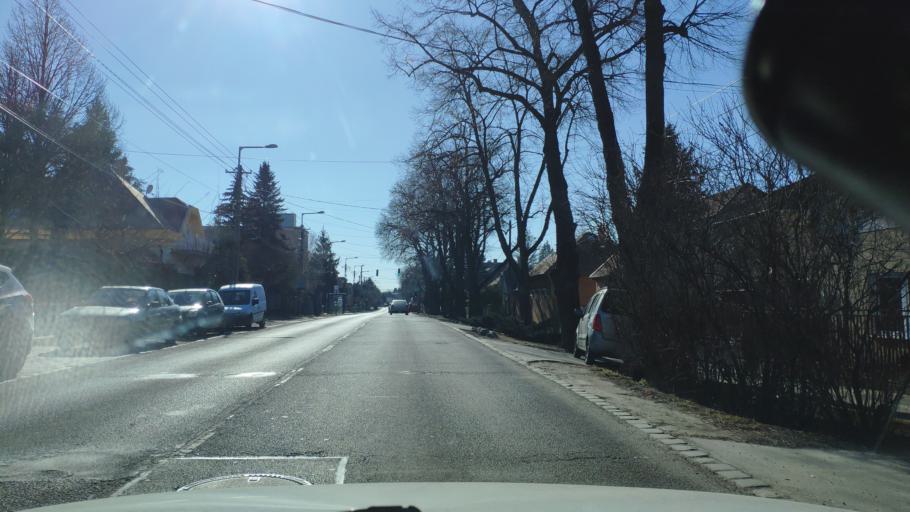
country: HU
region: Budapest
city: Budapest XVI. keruelet
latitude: 47.5072
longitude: 19.1808
